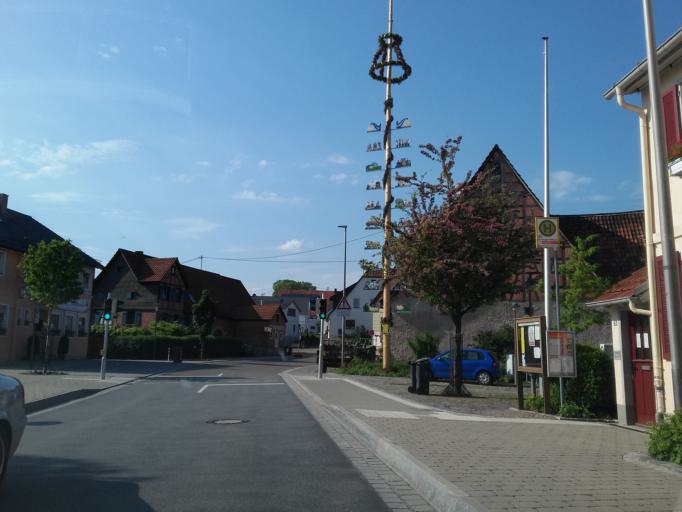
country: DE
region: Baden-Wuerttemberg
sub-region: Regierungsbezirk Stuttgart
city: Backnang
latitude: 48.9200
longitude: 9.4431
